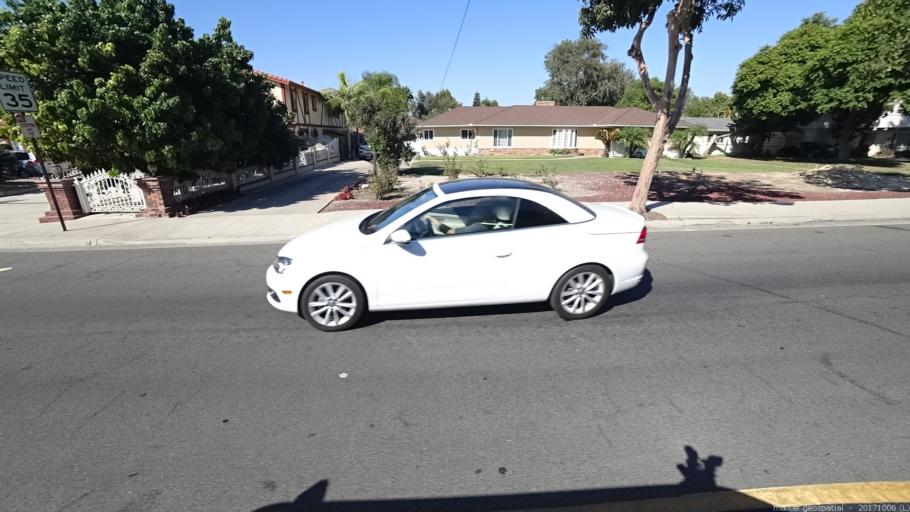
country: US
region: California
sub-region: Orange County
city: Garden Grove
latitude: 33.7815
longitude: -117.9335
